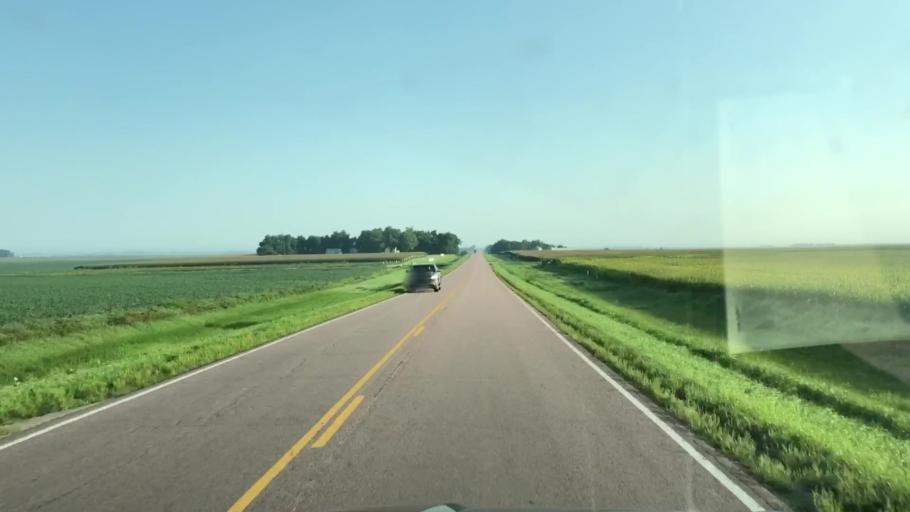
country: US
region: Iowa
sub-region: Lyon County
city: George
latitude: 43.2852
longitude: -95.9996
